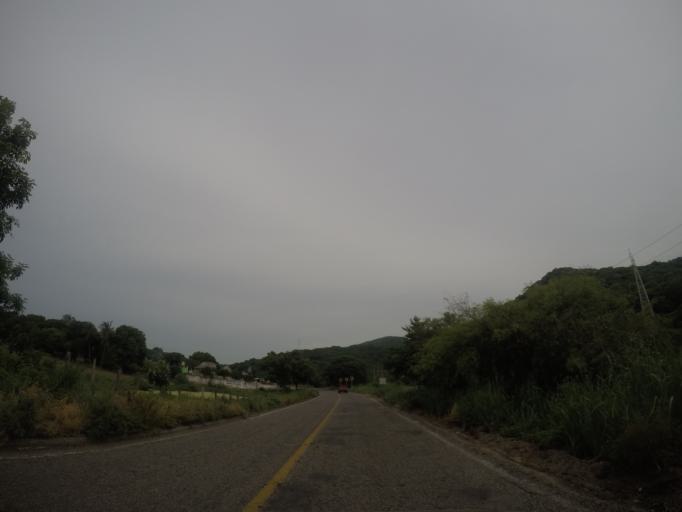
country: MX
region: Oaxaca
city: San Pedro Mixtepec
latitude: 15.9564
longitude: -97.2104
